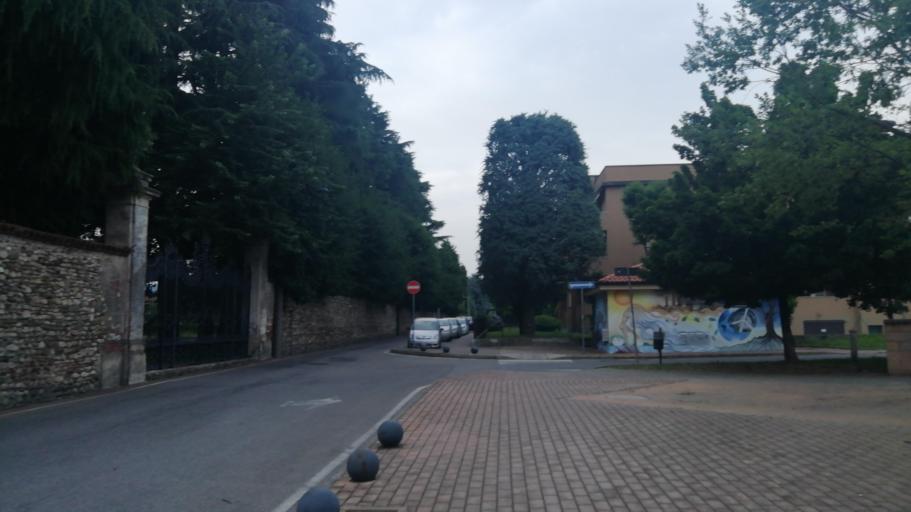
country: IT
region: Lombardy
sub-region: Provincia di Lecco
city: Osnago
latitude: 45.6785
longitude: 9.3932
